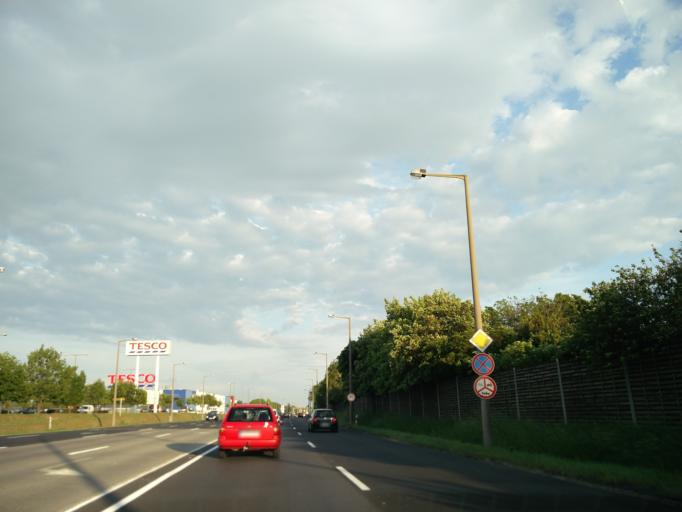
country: HU
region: Fejer
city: Szekesfehervar
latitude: 47.2086
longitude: 18.4239
